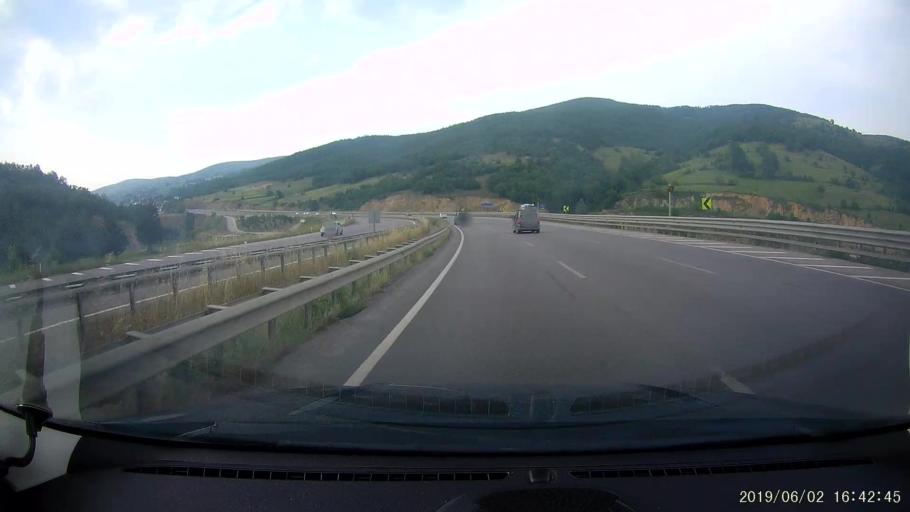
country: TR
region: Samsun
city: Kavak
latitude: 41.1229
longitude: 36.1377
